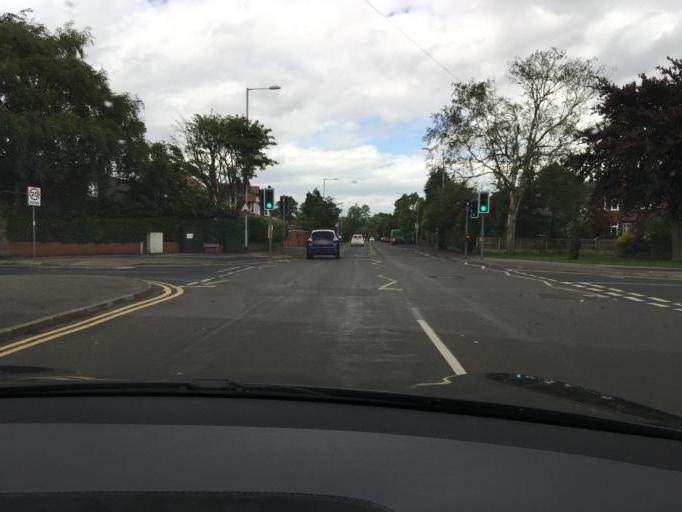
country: GB
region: England
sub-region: Borough of Stockport
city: Hazel Grove
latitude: 53.3718
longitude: -2.1239
